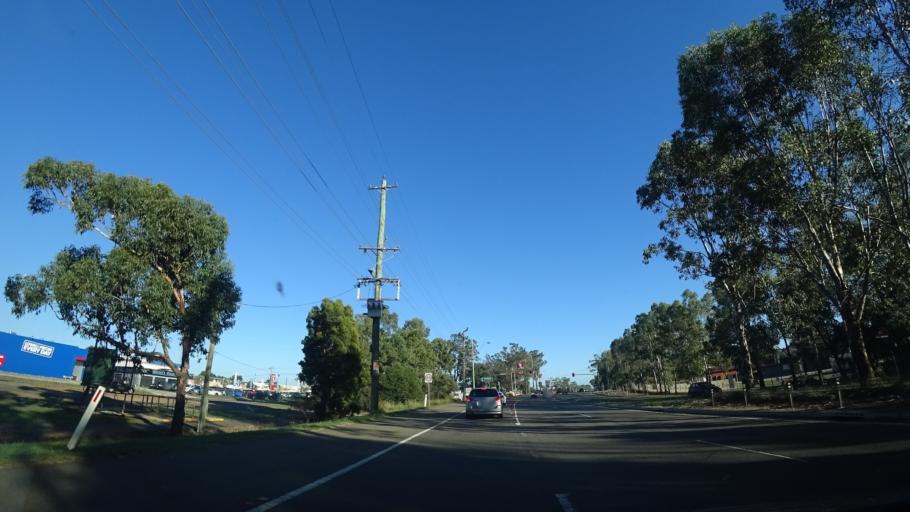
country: AU
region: New South Wales
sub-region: Hawkesbury
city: South Windsor
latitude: -33.6266
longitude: 150.8394
